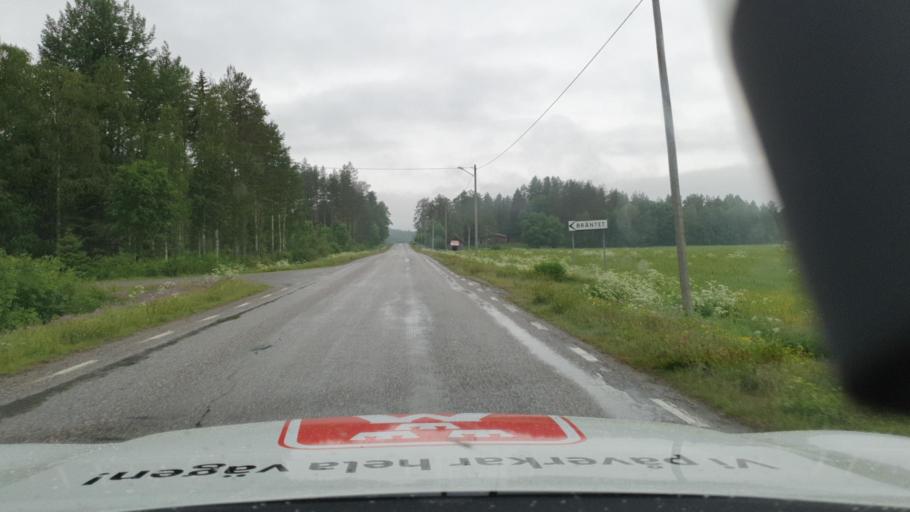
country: SE
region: Vaesterbotten
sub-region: Nordmalings Kommun
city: Nordmaling
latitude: 63.7933
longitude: 19.5377
